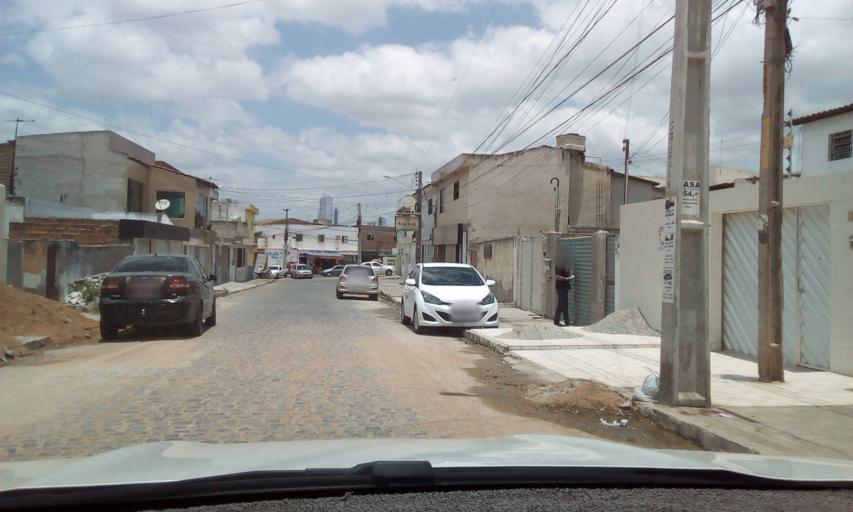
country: BR
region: Pernambuco
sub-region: Caruaru
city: Caruaru
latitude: -8.2688
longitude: -35.9867
